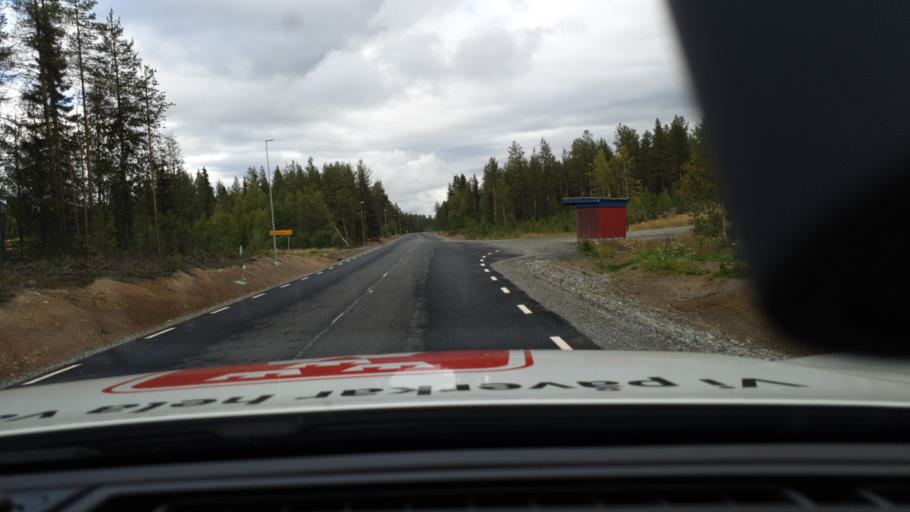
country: SE
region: Norrbotten
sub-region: Gallivare Kommun
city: Gaellivare
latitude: 66.8787
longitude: 21.2512
